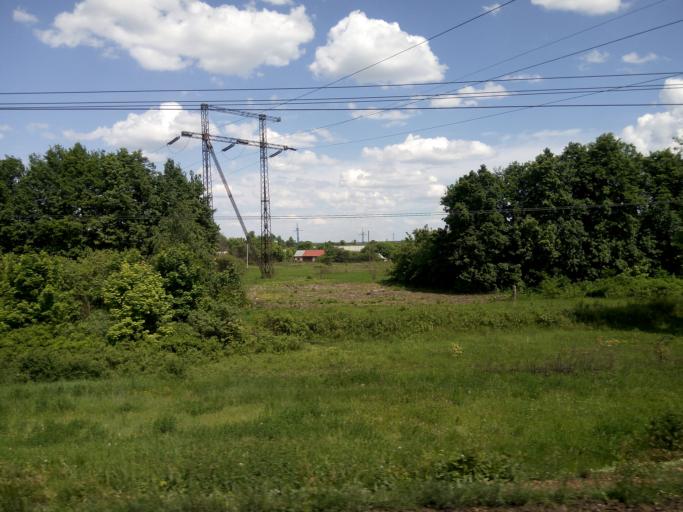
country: RU
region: Moskovskaya
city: Yam
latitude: 55.4848
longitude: 37.7353
